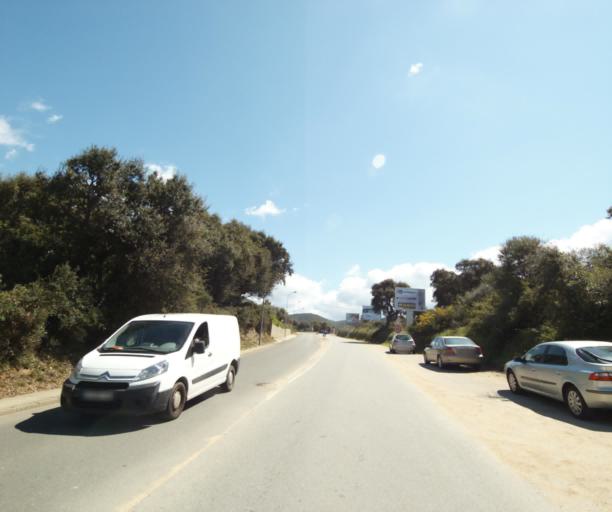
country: FR
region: Corsica
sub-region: Departement de la Corse-du-Sud
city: Propriano
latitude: 41.6694
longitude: 8.9166
